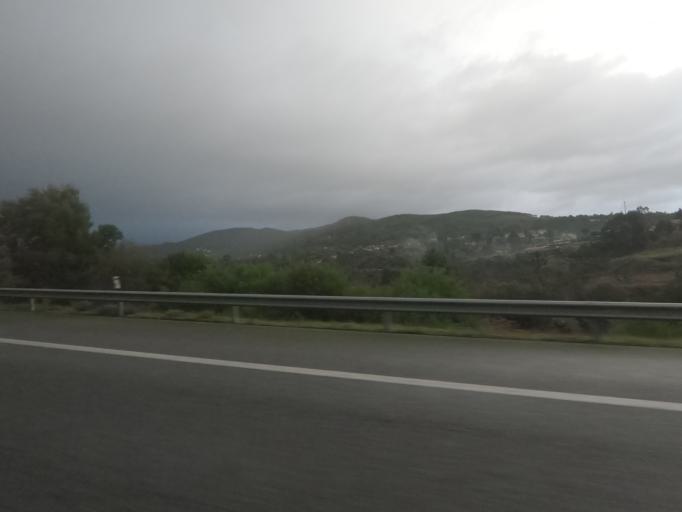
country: PT
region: Viana do Castelo
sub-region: Ponte de Lima
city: Ponte de Lima
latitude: 41.8138
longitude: -8.5994
